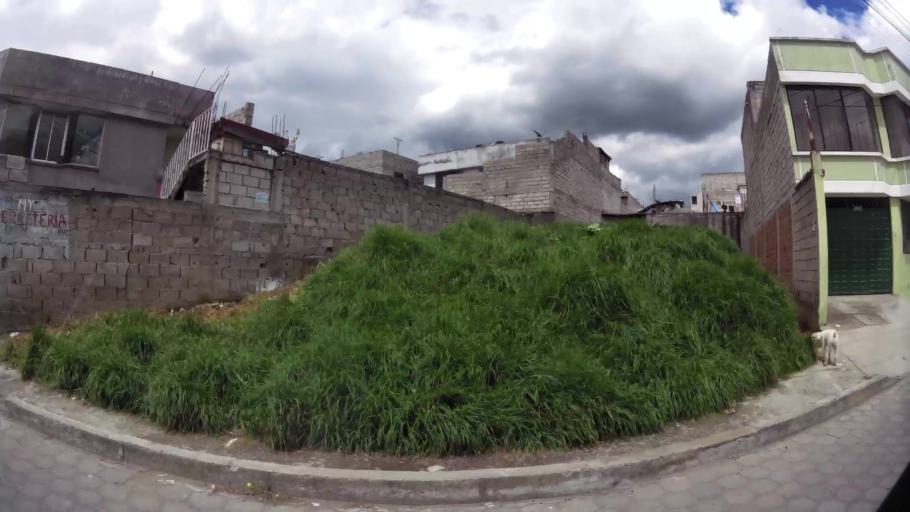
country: EC
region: Pichincha
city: Sangolqui
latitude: -0.3345
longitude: -78.5350
